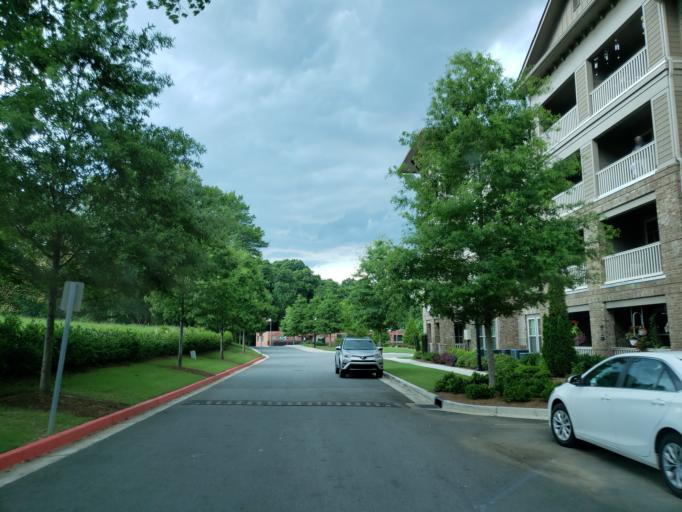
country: US
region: Georgia
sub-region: Cobb County
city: Acworth
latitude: 34.0680
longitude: -84.6789
